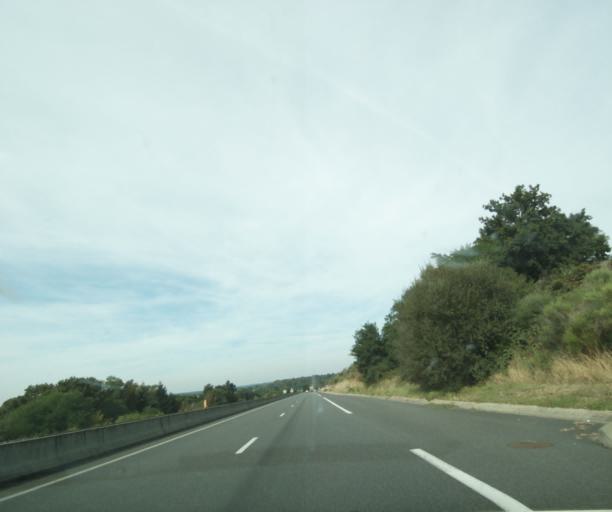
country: FR
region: Auvergne
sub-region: Departement de l'Allier
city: Lapalisse
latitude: 46.2232
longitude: 3.6586
